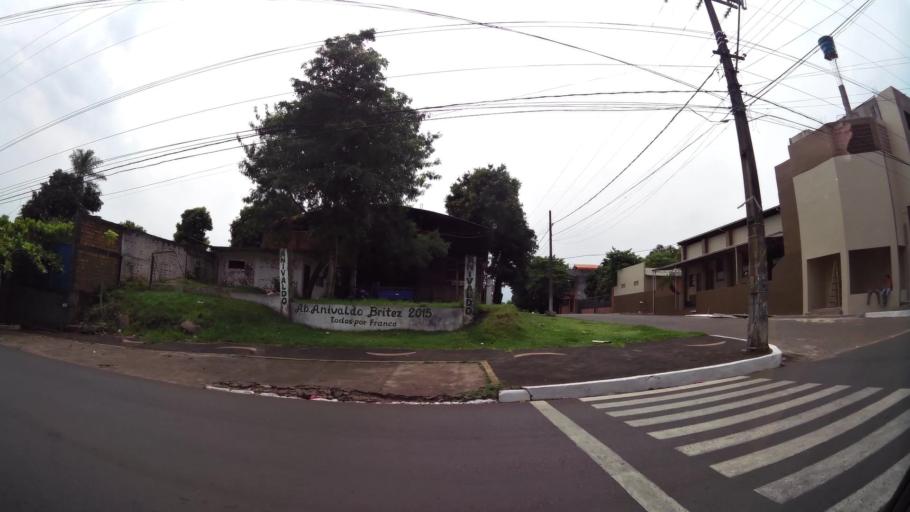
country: PY
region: Alto Parana
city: Presidente Franco
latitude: -25.5509
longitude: -54.6080
